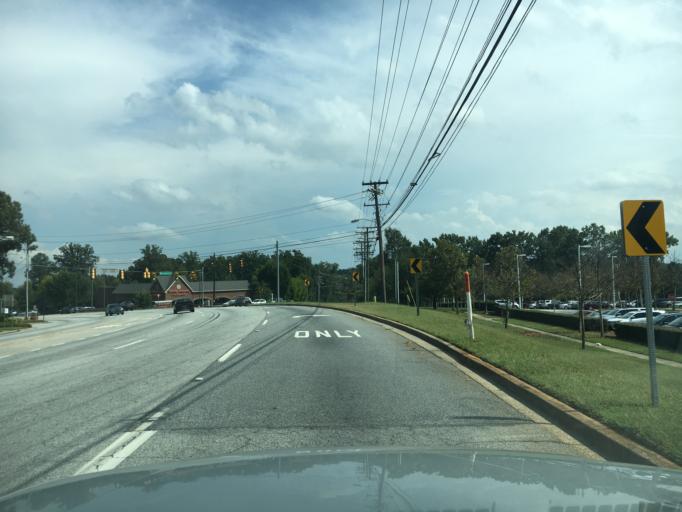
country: US
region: South Carolina
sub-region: Greenville County
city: Wade Hampton
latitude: 34.8554
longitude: -82.3224
